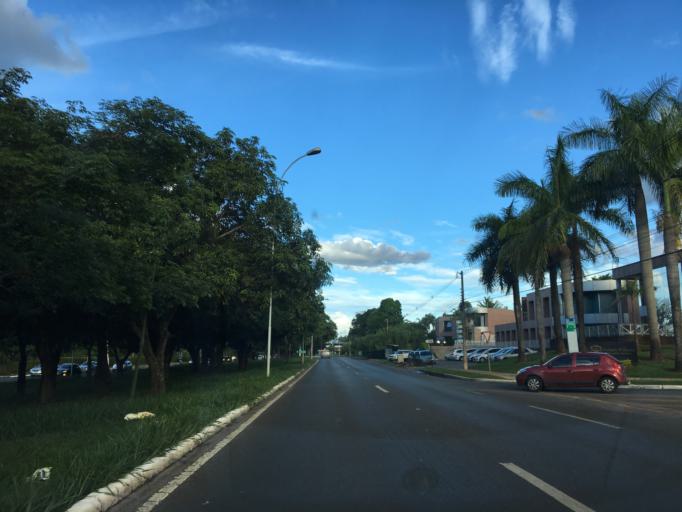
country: BR
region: Federal District
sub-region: Brasilia
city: Brasilia
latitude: -15.8570
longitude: -47.9201
